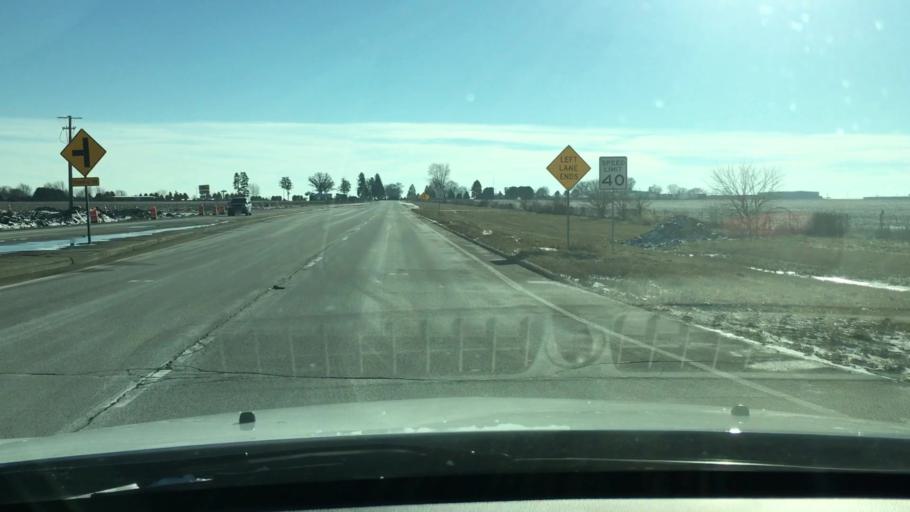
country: US
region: Illinois
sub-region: Ogle County
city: Rochelle
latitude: 41.8986
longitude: -89.0686
